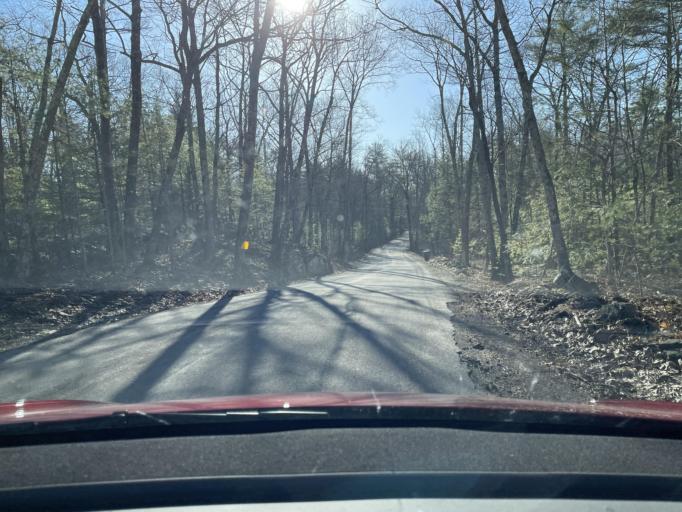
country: US
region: New York
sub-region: Ulster County
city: Zena
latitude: 42.0626
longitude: -74.0656
